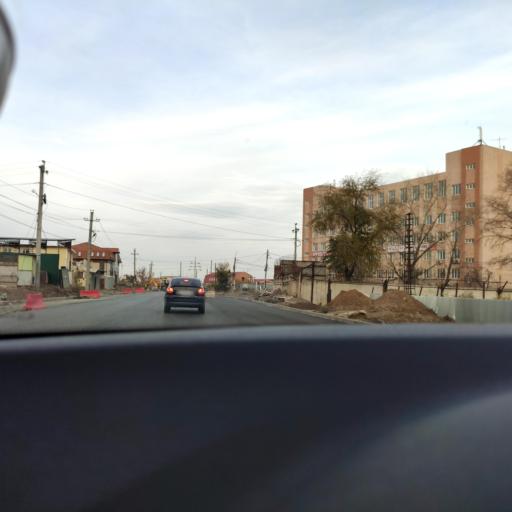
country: RU
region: Samara
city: Samara
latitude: 53.1837
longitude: 50.2154
